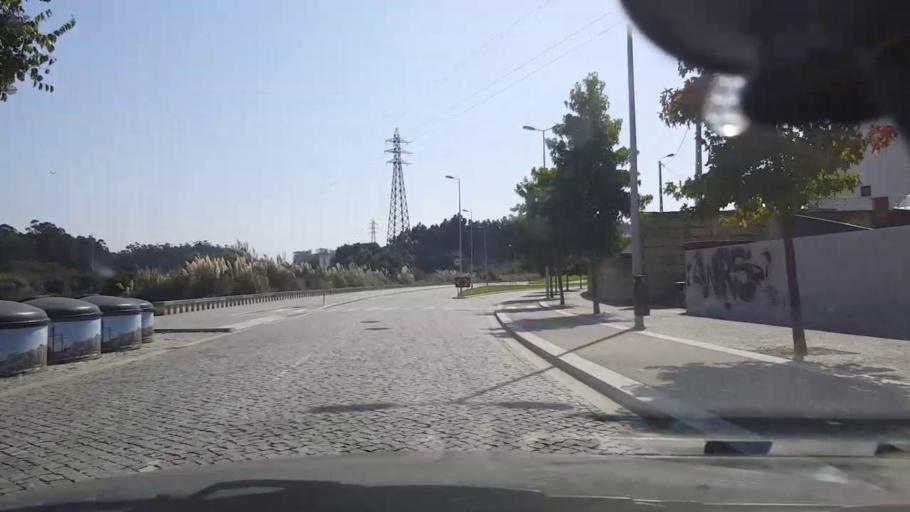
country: PT
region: Porto
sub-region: Vila do Conde
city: Vila do Conde
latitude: 41.3553
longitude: -8.7311
